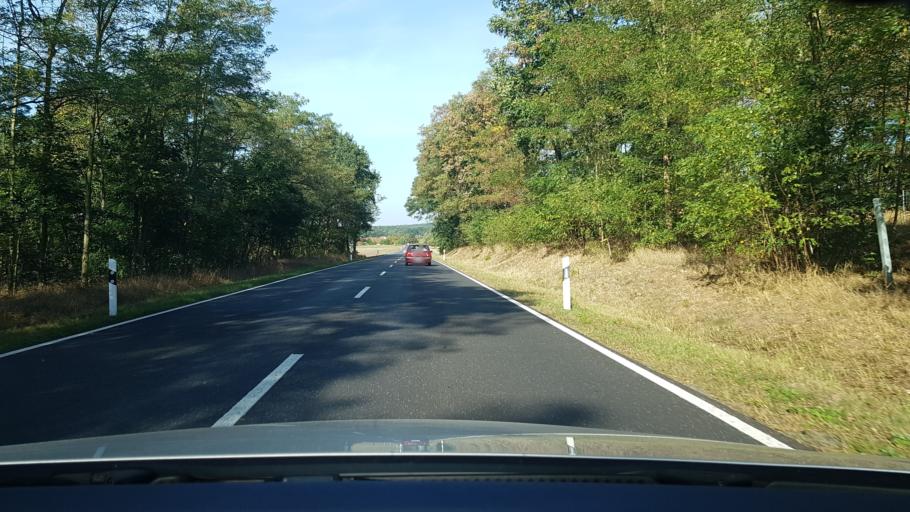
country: DE
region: Brandenburg
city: Mixdorf
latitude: 52.1385
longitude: 14.4264
